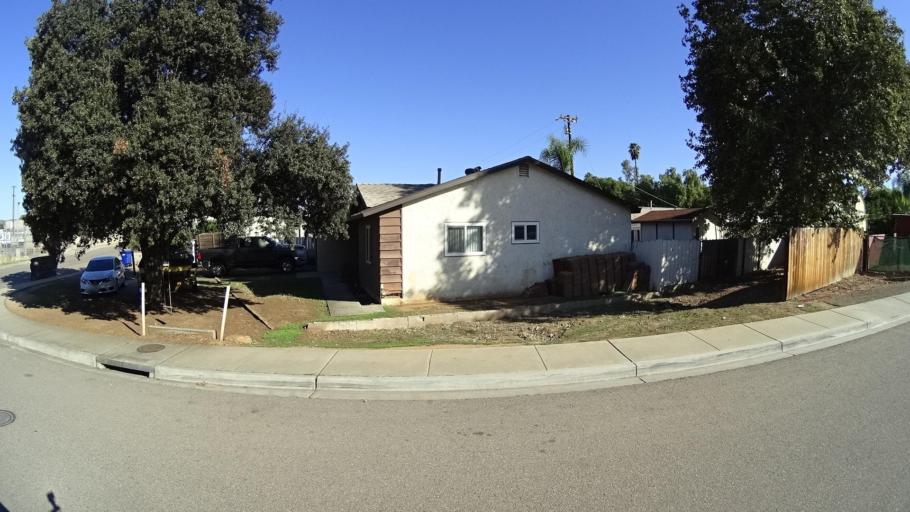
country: US
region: California
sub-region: San Diego County
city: Lakeside
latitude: 32.8563
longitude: -116.9200
